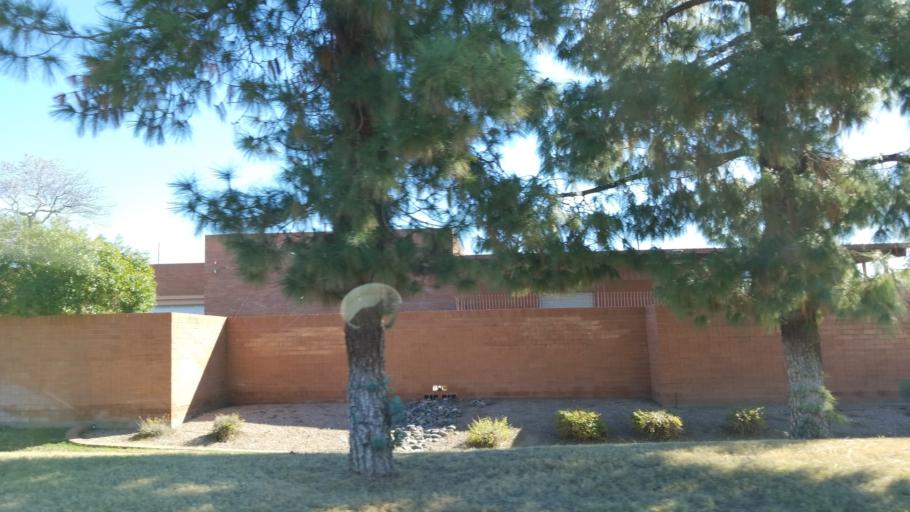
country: US
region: Arizona
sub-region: Maricopa County
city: Glendale
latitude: 33.6503
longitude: -112.1171
